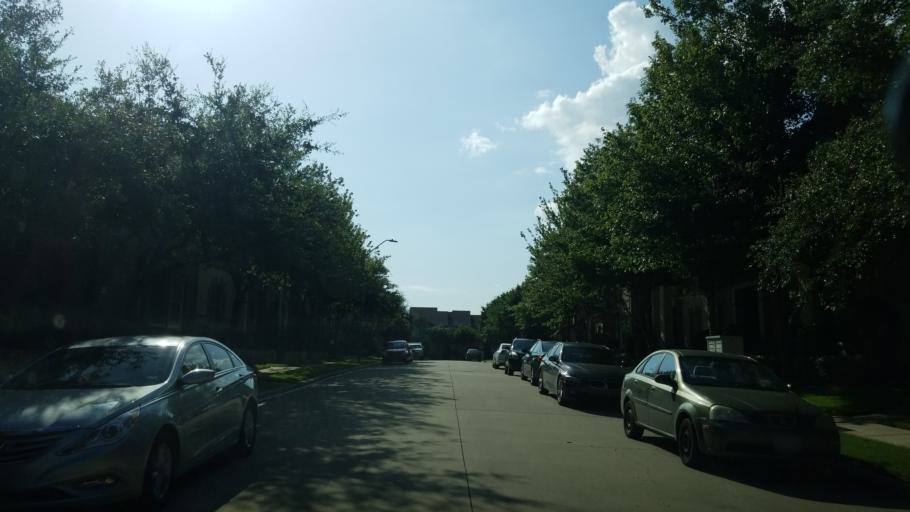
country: US
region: Texas
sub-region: Dallas County
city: Coppell
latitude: 32.9233
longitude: -96.9698
